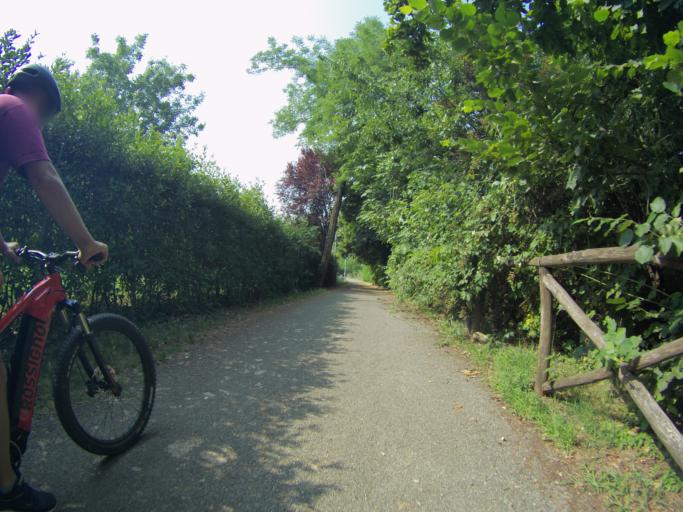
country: IT
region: Emilia-Romagna
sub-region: Provincia di Reggio Emilia
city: Pratissolo
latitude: 44.5902
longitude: 10.6742
